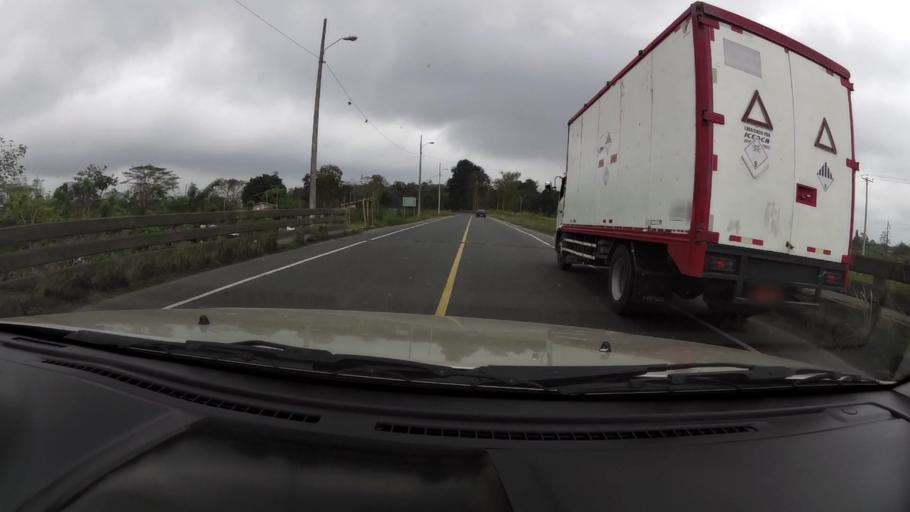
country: EC
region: Guayas
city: Balao
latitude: -2.9327
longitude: -79.7131
